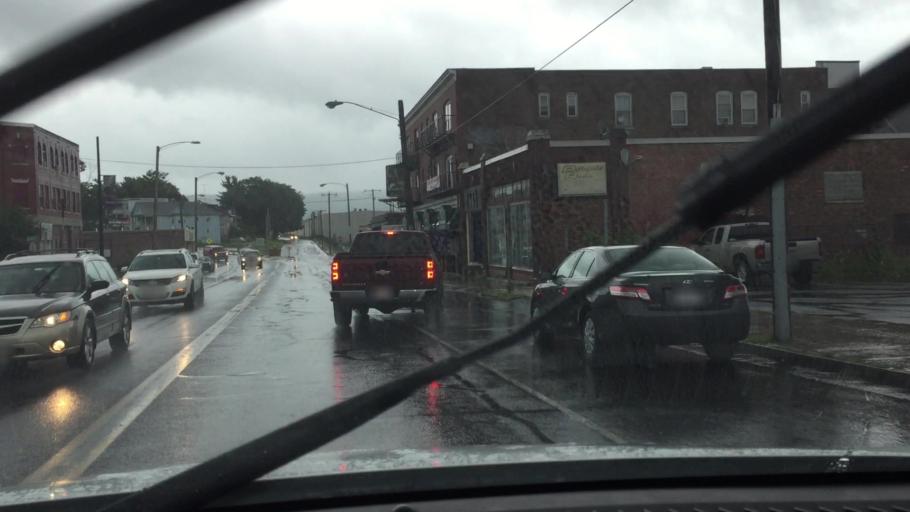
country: US
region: Massachusetts
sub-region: Berkshire County
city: Pittsfield
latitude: 42.4566
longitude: -73.2358
